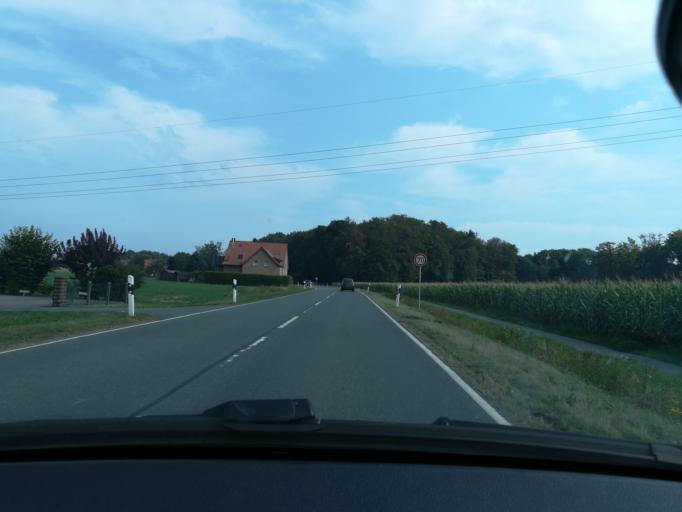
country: DE
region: Lower Saxony
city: Melle
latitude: 52.1711
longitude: 8.3356
